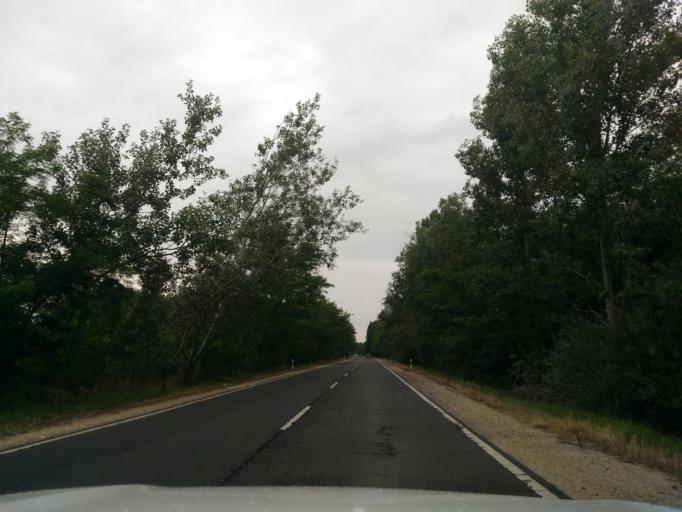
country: HU
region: Pest
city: Alsonemedi
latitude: 47.2897
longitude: 19.1902
